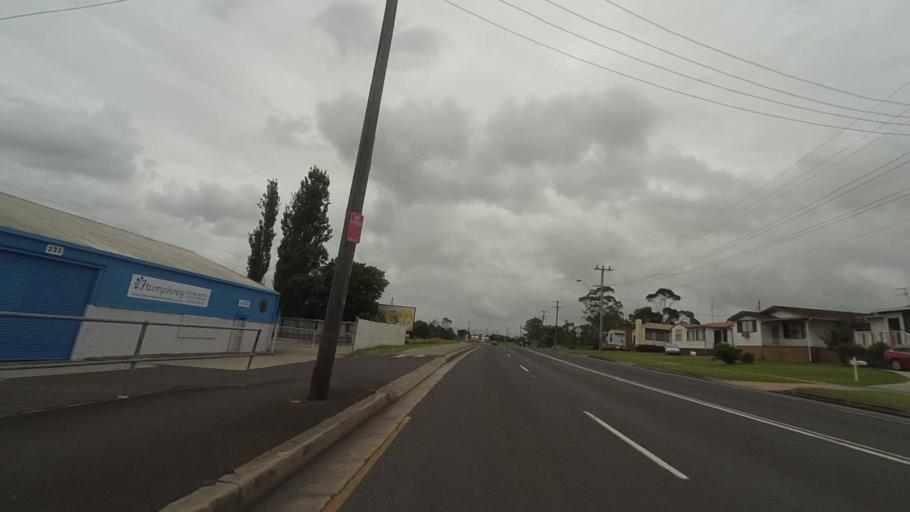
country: AU
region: New South Wales
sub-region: Wollongong
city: Cordeaux Heights
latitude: -34.4622
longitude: 150.8383
